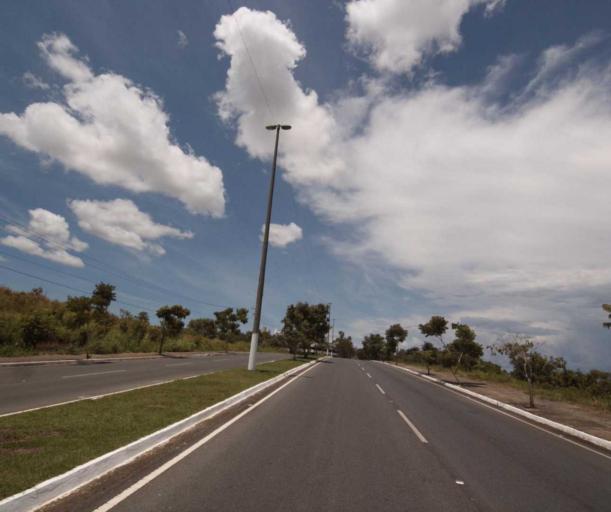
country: BR
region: Mato Grosso
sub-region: Cuiaba
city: Cuiaba
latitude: -15.5700
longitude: -56.1073
